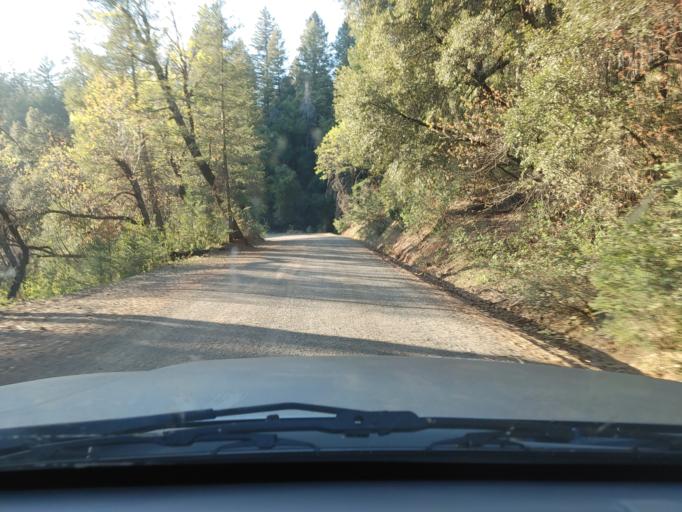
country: US
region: California
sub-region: Shasta County
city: Bella Vista
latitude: 40.8211
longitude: -122.0094
